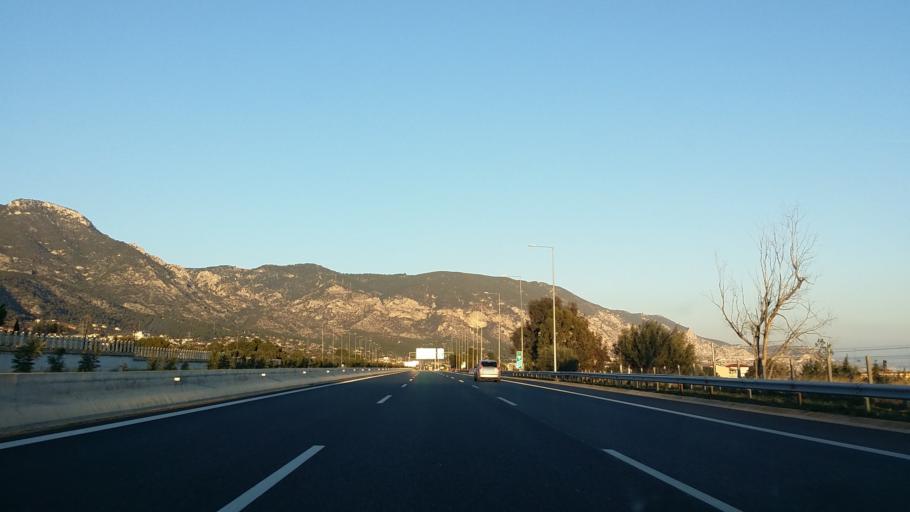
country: GR
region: Attica
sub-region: Nomarchia Dytikis Attikis
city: Kineta
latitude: 37.9614
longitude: 23.1922
